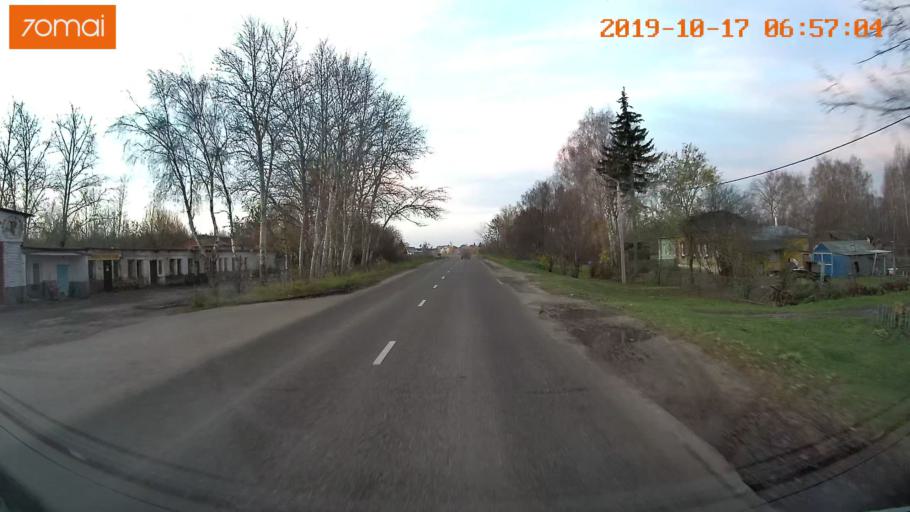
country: RU
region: Vladimir
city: Suzdal'
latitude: 56.4399
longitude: 40.4423
